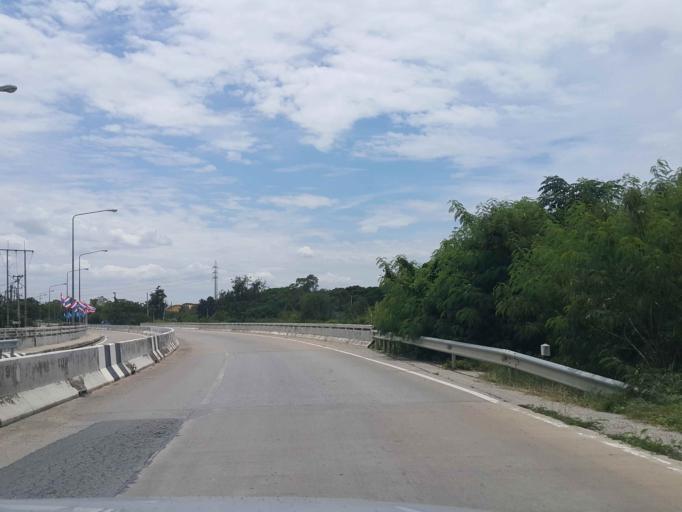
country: TH
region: Chiang Mai
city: Saraphi
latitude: 18.7362
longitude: 99.0403
